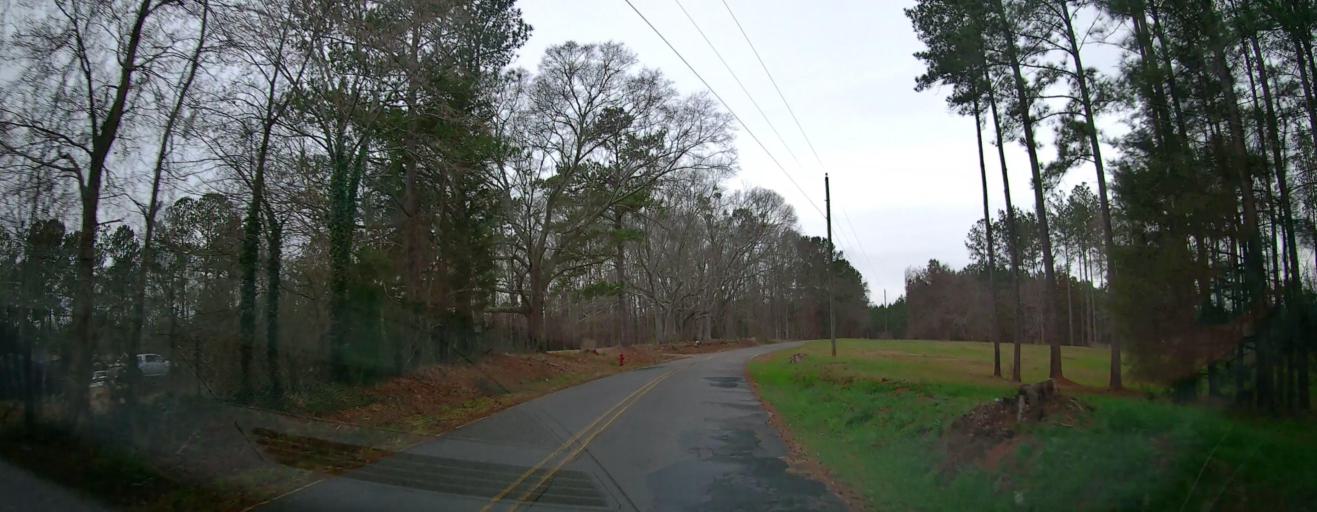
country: US
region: Georgia
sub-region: Monroe County
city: Forsyth
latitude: 33.0134
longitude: -83.8267
